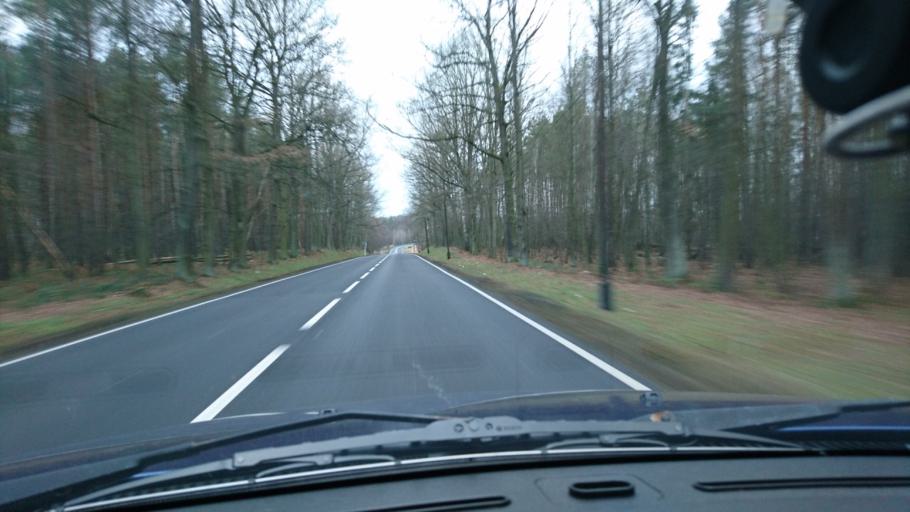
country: PL
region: Opole Voivodeship
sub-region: Powiat kluczborski
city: Kluczbork
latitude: 50.9509
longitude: 18.3123
